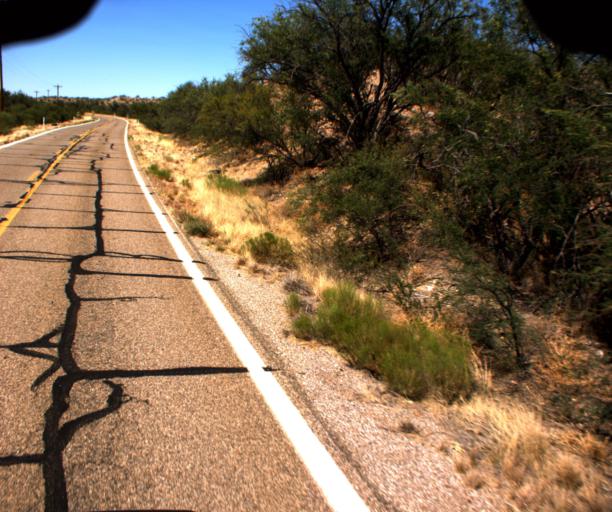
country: US
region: Arizona
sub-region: Pima County
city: Three Points
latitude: 31.8668
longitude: -111.3967
